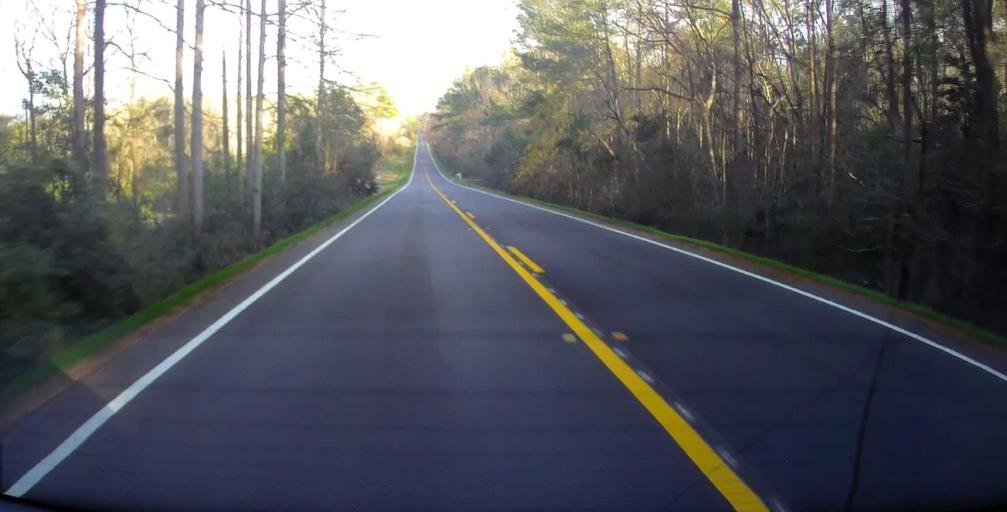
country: US
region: Georgia
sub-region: Harris County
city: Hamilton
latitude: 32.7495
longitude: -84.9221
